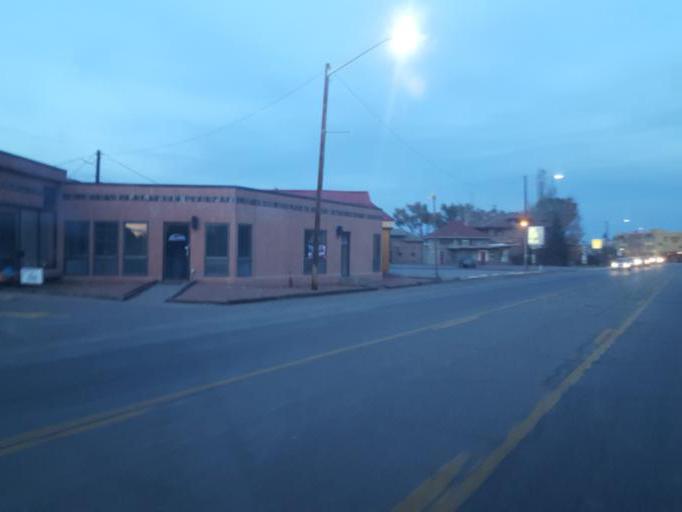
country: US
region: Colorado
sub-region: Rio Grande County
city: Monte Vista
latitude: 37.5795
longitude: -106.1428
